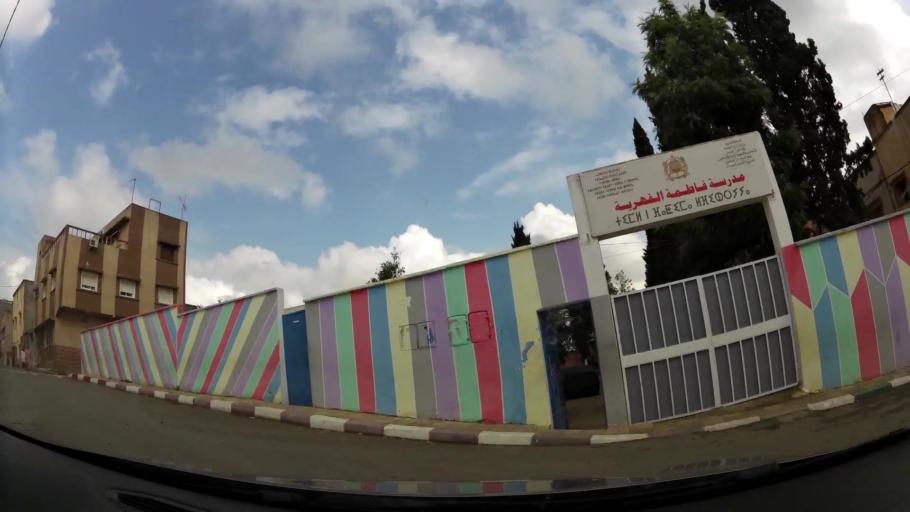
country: MA
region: Rabat-Sale-Zemmour-Zaer
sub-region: Khemisset
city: Tiflet
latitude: 33.8968
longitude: -6.3097
